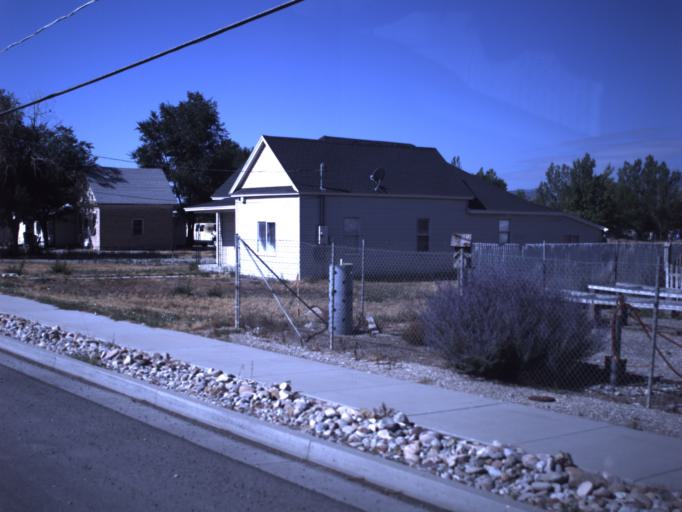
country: US
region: Utah
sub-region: Sanpete County
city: Centerfield
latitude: 39.1336
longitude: -111.8192
